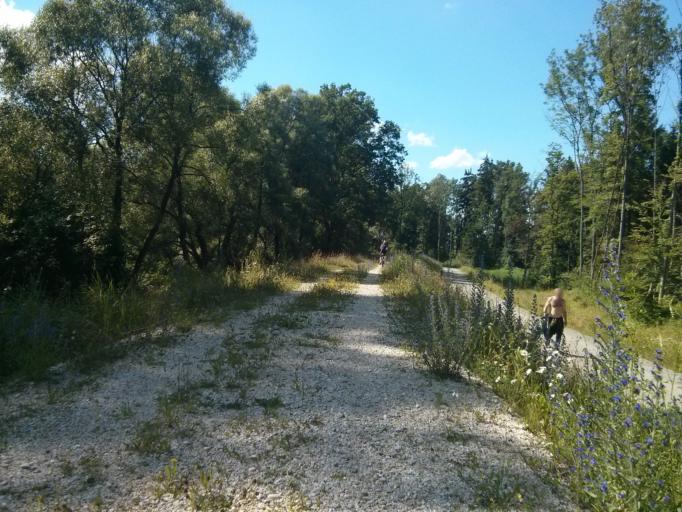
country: DE
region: Bavaria
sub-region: Lower Bavaria
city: Moos
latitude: 48.7873
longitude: 12.9375
